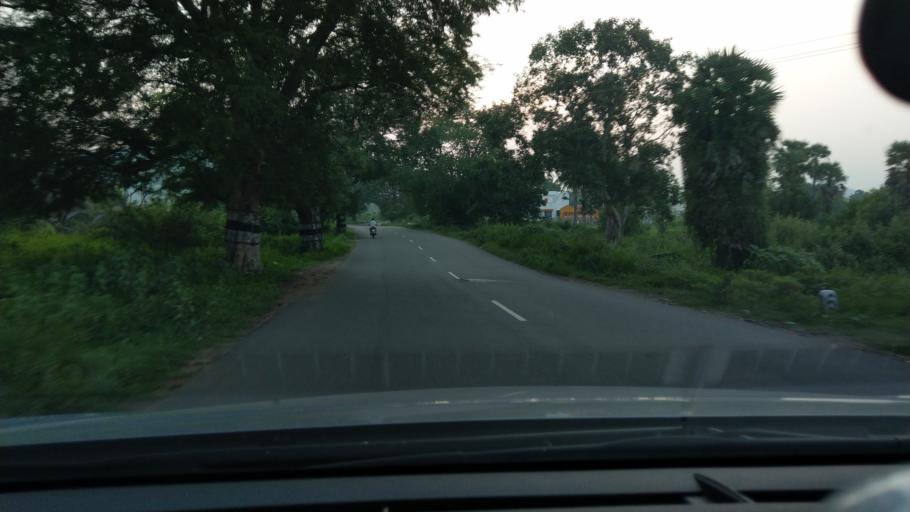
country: IN
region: Tamil Nadu
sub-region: Salem
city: Attur
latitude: 11.5954
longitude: 78.5699
